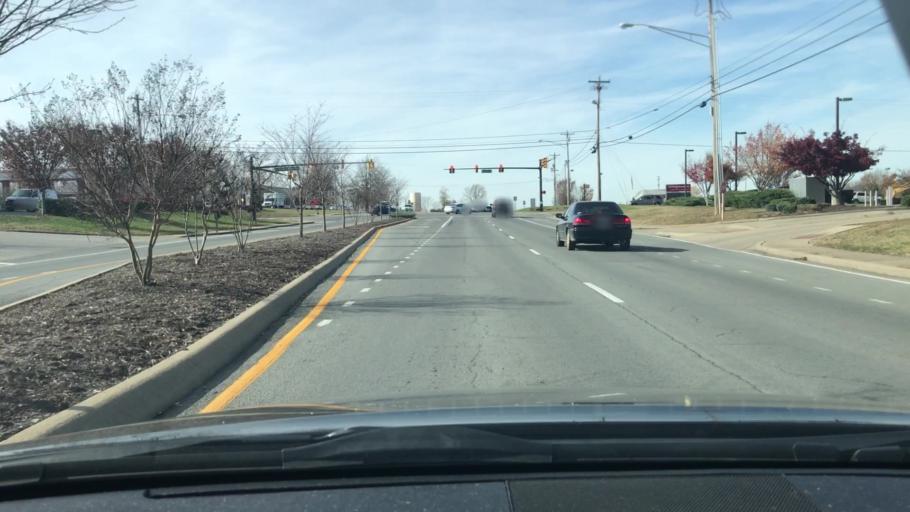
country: US
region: Tennessee
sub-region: Sumner County
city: White House
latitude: 36.4687
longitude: -86.6642
